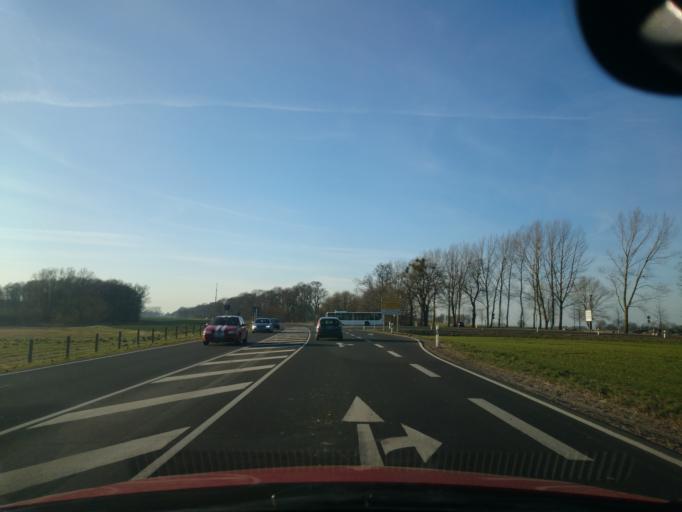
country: DE
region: Mecklenburg-Vorpommern
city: Brandshagen
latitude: 54.2155
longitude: 13.2436
